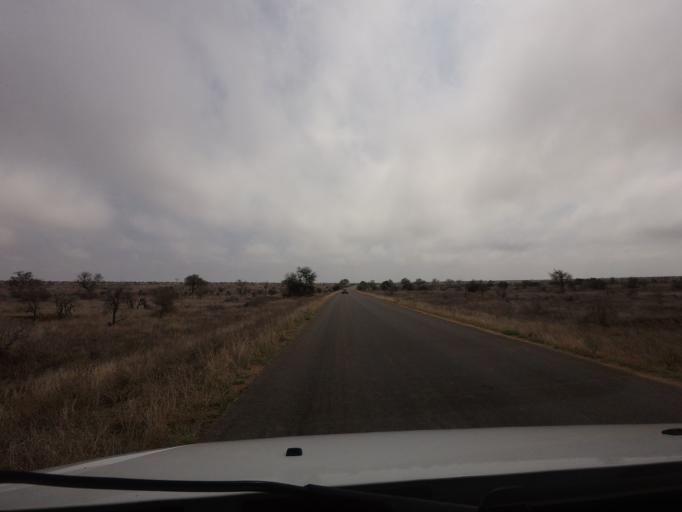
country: ZA
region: Limpopo
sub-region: Mopani District Municipality
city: Phalaborwa
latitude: -24.1976
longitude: 31.7188
